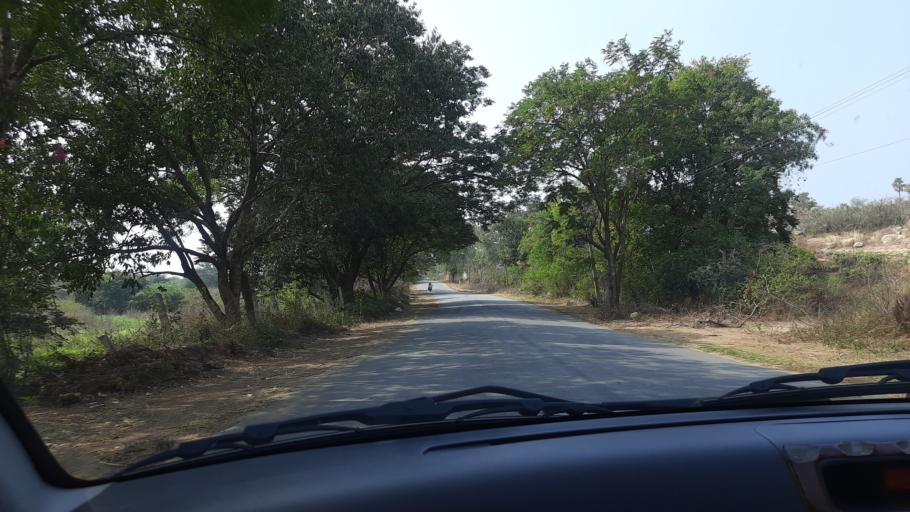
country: IN
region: Telangana
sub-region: Rangareddi
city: Lal Bahadur Nagar
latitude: 17.2753
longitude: 78.6634
